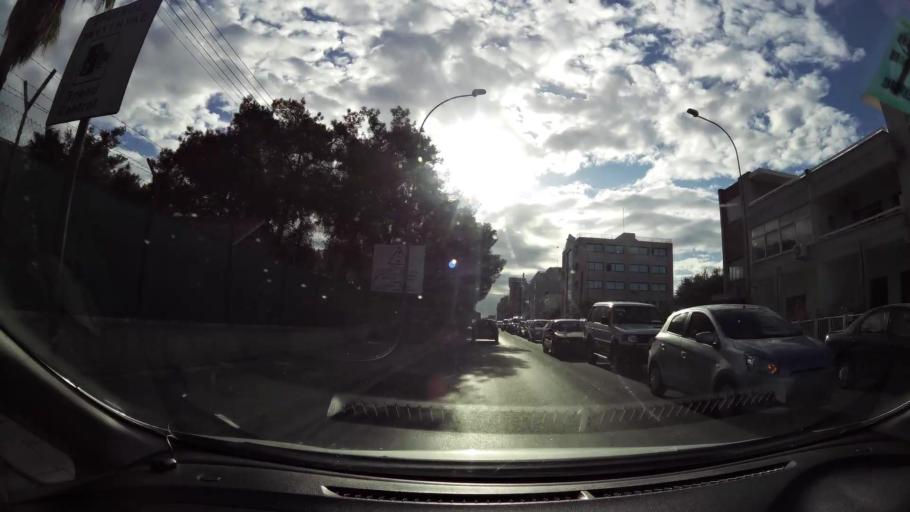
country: CY
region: Lefkosia
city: Nicosia
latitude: 35.1501
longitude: 33.3478
